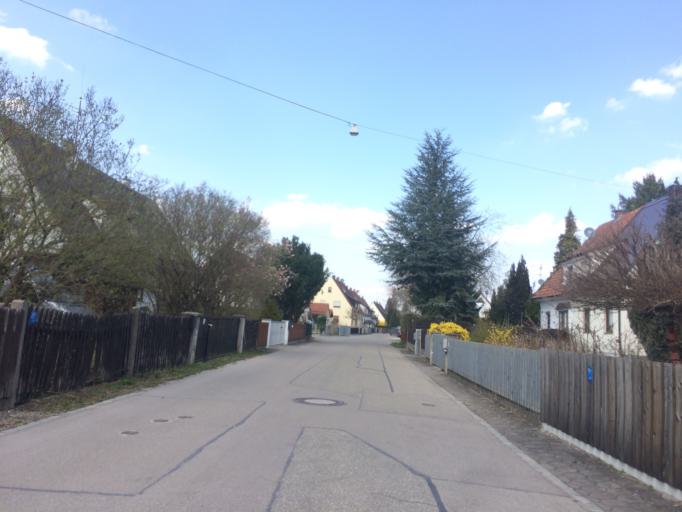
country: DE
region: Bavaria
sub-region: Swabia
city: Augsburg
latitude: 48.4003
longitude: 10.8964
